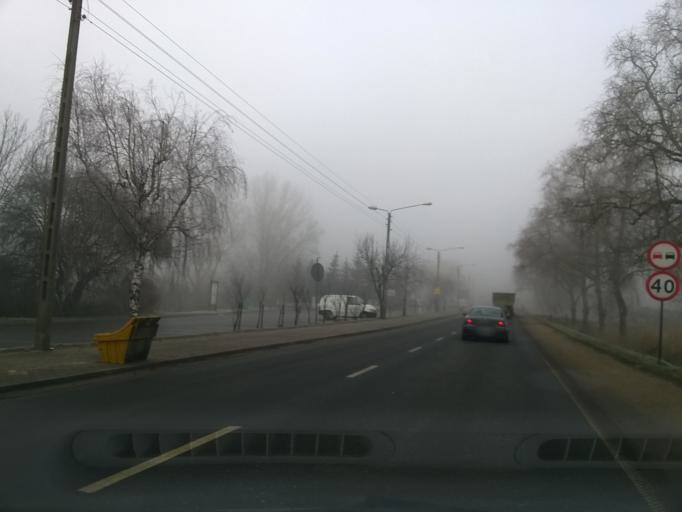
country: PL
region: Kujawsko-Pomorskie
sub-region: Powiat nakielski
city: Naklo nad Notecia
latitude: 53.1344
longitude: 17.6021
